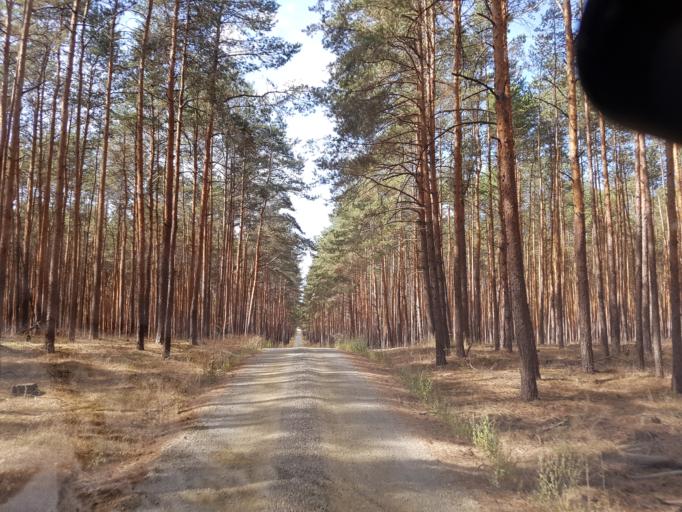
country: DE
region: Brandenburg
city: Sonnewalde
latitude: 51.7585
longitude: 13.6424
